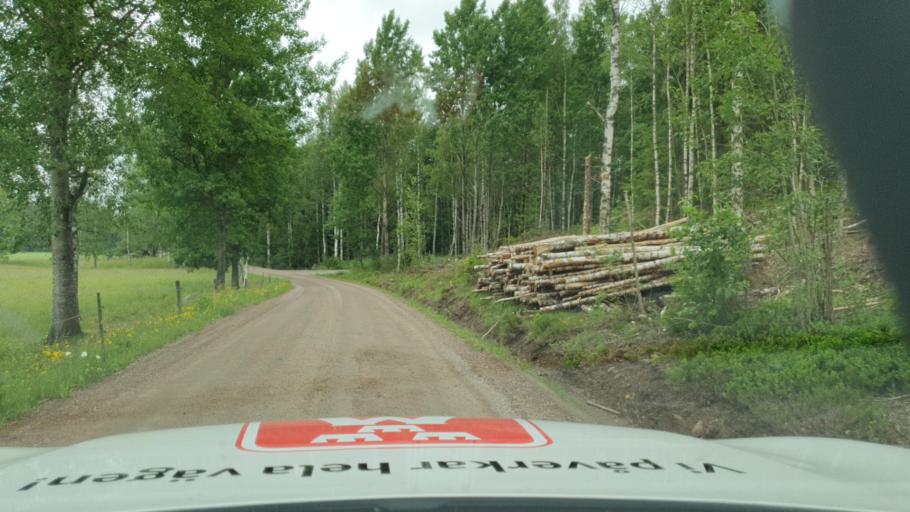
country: SE
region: Vaermland
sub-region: Filipstads Kommun
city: Filipstad
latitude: 59.5749
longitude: 13.9594
